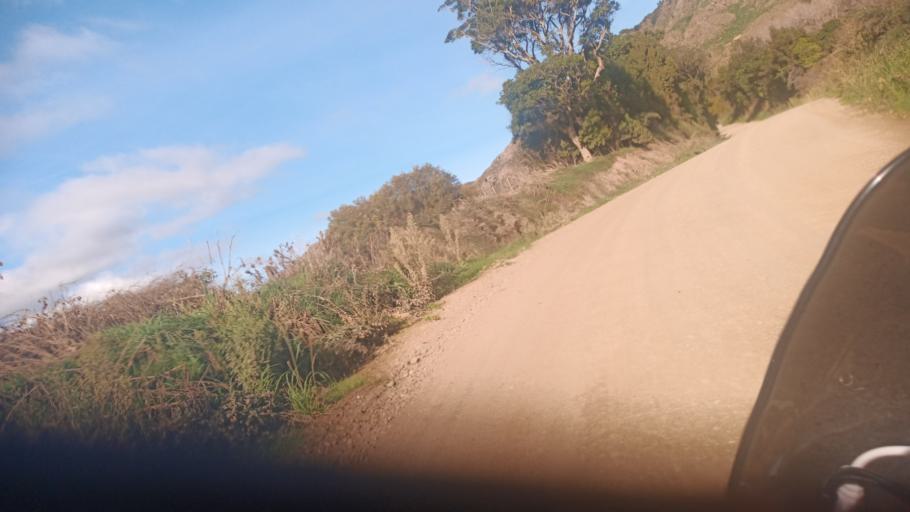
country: NZ
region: Gisborne
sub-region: Gisborne District
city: Gisborne
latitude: -38.4288
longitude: 177.5615
